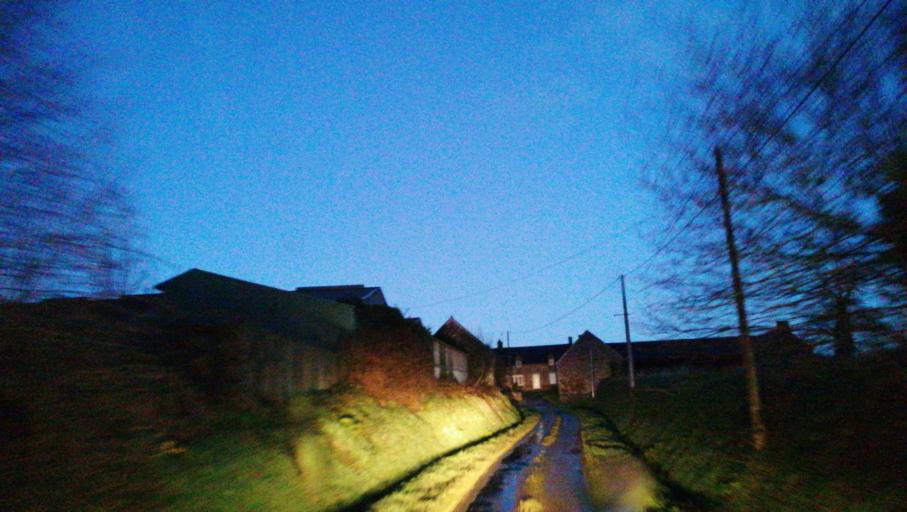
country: FR
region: Brittany
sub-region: Departement des Cotes-d'Armor
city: Plelo
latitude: 48.5635
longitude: -2.9682
